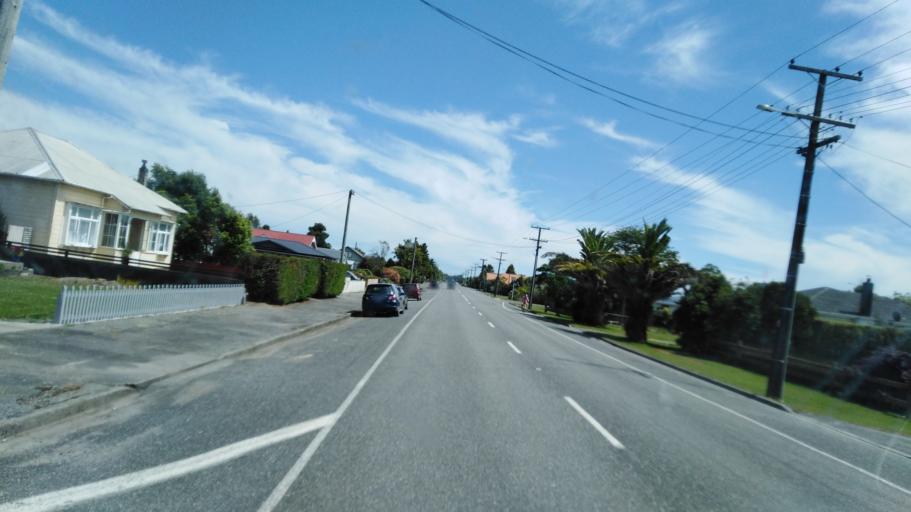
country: NZ
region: West Coast
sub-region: Buller District
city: Westport
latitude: -41.7524
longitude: 171.6229
